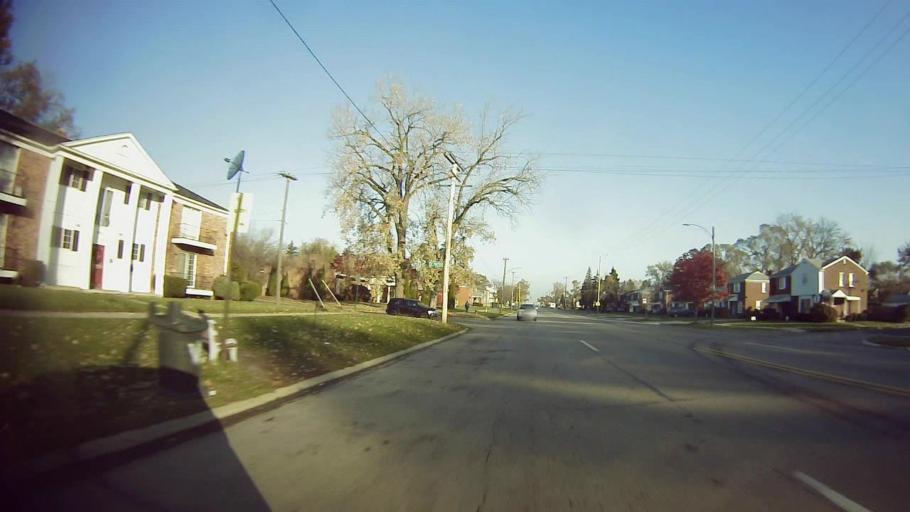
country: US
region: Michigan
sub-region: Oakland County
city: Oak Park
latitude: 42.4355
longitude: -83.2002
